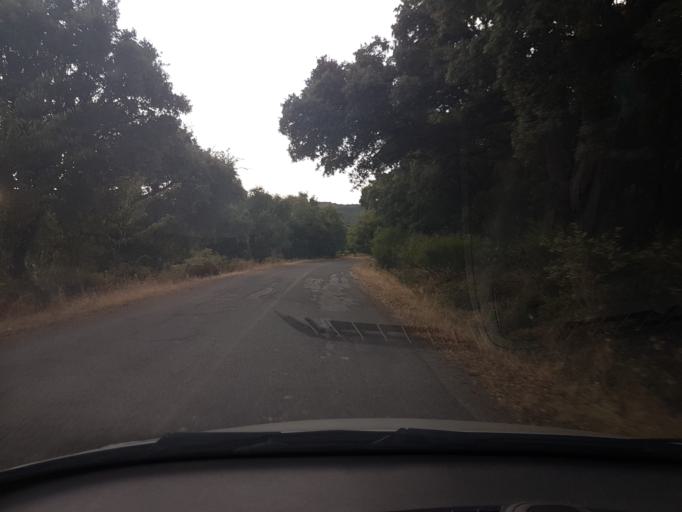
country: IT
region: Sardinia
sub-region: Provincia di Oristano
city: Seneghe
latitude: 40.1085
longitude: 8.6217
